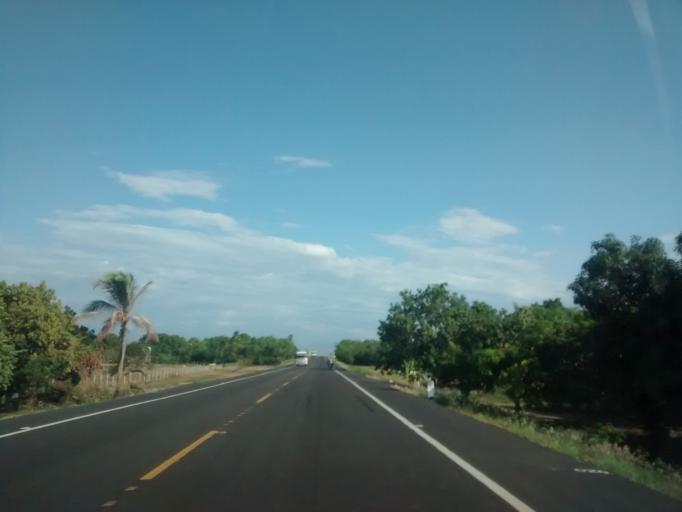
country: CO
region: Tolima
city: Espinal
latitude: 4.1567
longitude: -74.9165
